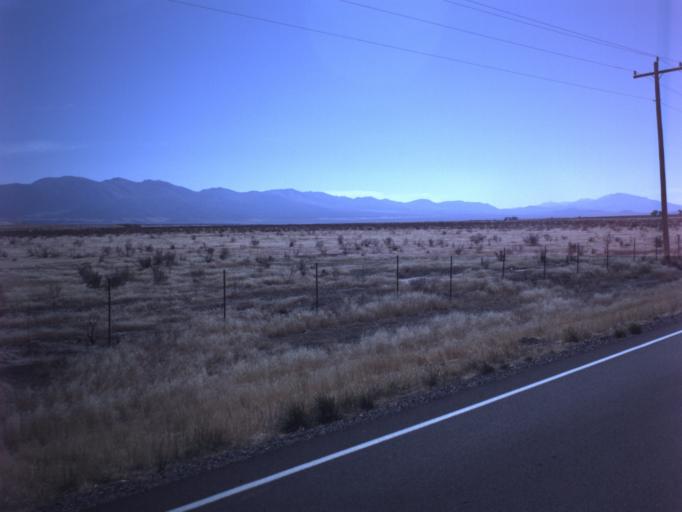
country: US
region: Utah
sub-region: Tooele County
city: Grantsville
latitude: 40.3656
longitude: -112.7461
